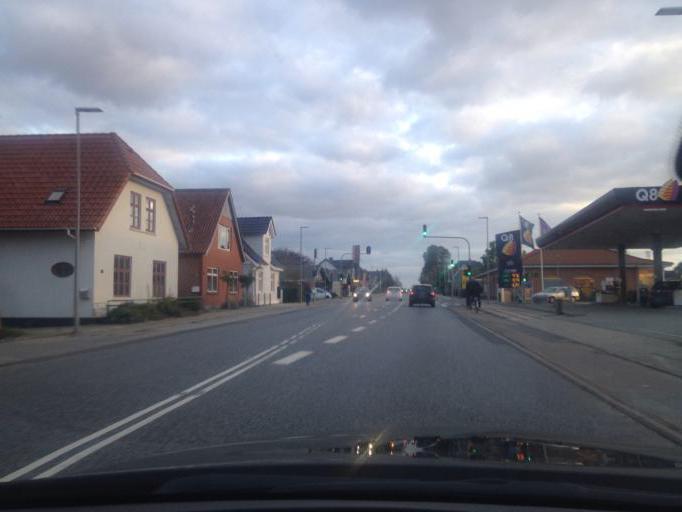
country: DK
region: South Denmark
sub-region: Kolding Kommune
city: Kolding
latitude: 55.4761
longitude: 9.4695
